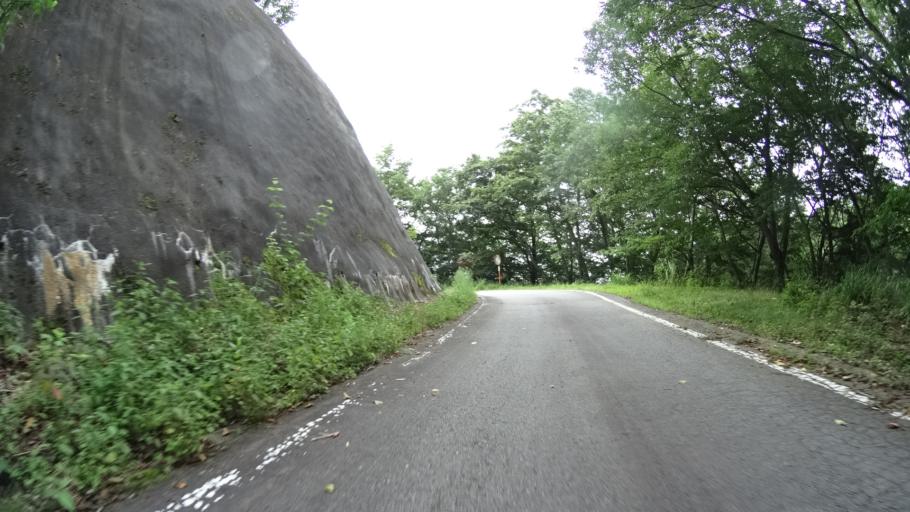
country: JP
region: Yamanashi
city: Nirasaki
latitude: 35.8074
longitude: 138.5425
